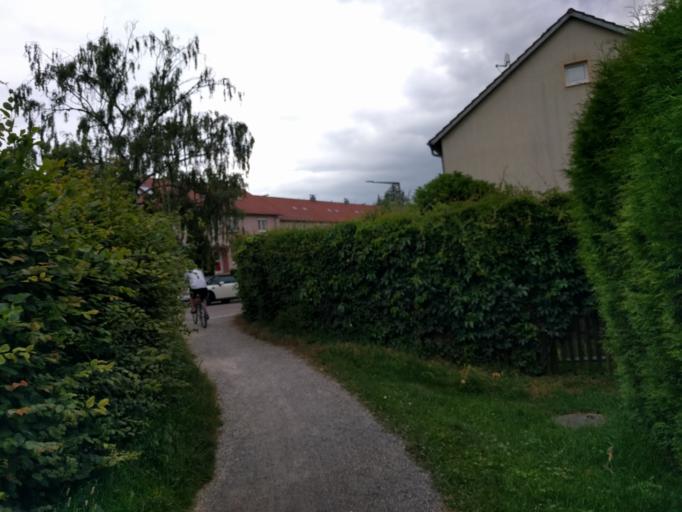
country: DE
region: Bavaria
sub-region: Upper Palatinate
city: Pentling
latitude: 49.0090
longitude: 12.0832
